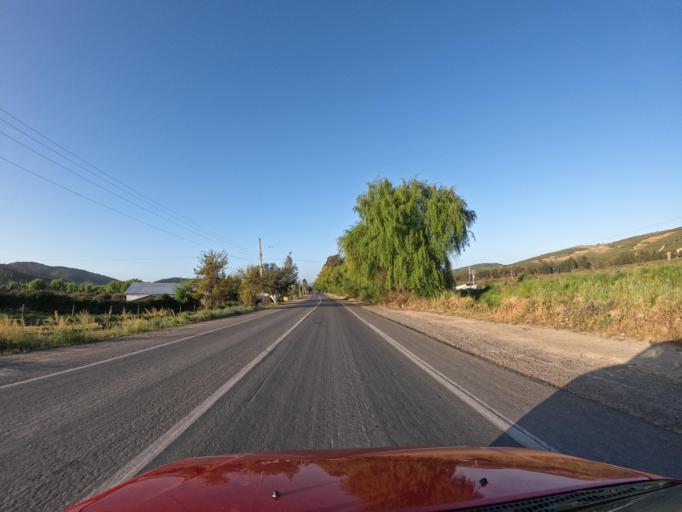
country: CL
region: O'Higgins
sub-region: Provincia de Colchagua
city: Santa Cruz
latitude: -34.3347
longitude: -71.3981
